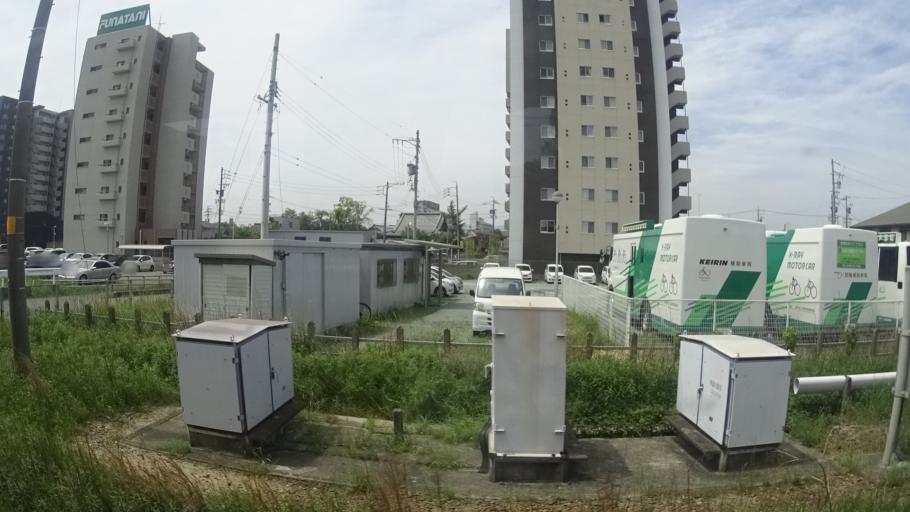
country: JP
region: Mie
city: Hisai-motomachi
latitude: 34.5791
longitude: 136.5341
